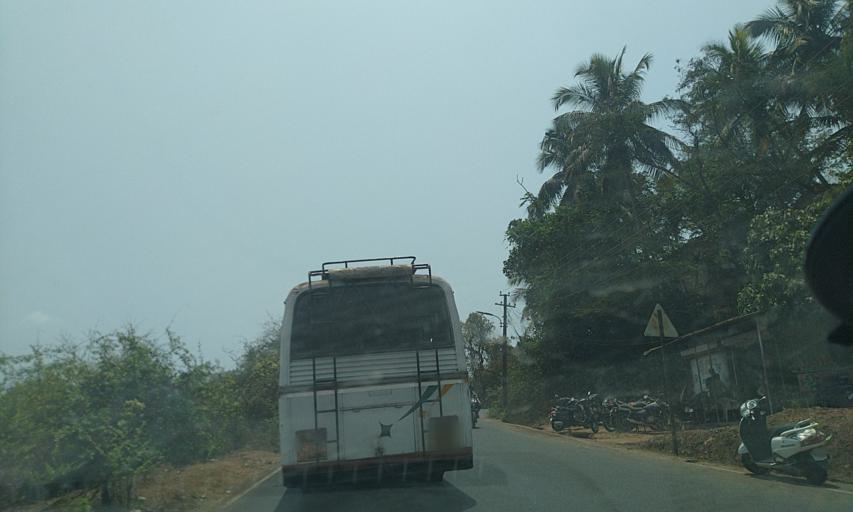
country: IN
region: Goa
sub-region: North Goa
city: Mapuca
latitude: 15.5964
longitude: 73.7991
